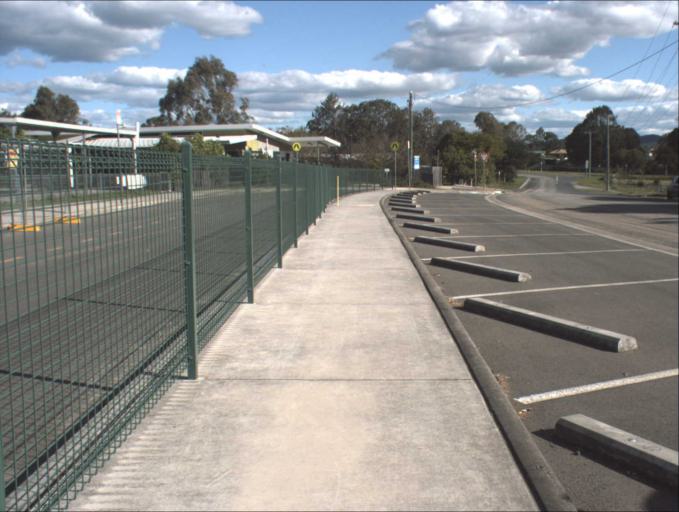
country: AU
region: Queensland
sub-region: Logan
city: Chambers Flat
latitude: -27.7635
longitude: 153.1052
